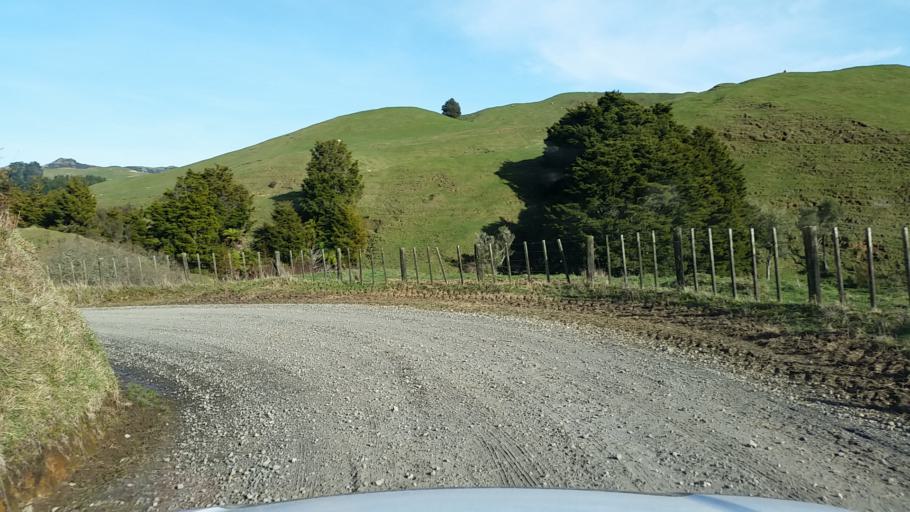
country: NZ
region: Taranaki
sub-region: South Taranaki District
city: Eltham
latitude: -39.3145
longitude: 174.5345
